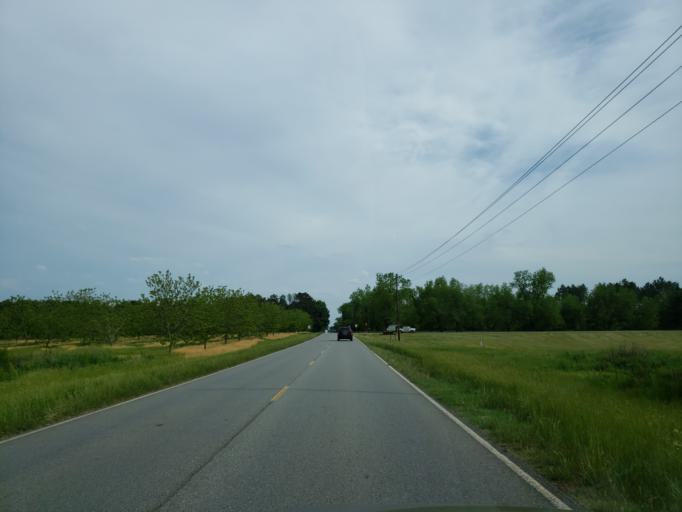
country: US
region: Georgia
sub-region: Dooly County
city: Vienna
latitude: 32.1555
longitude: -83.8818
